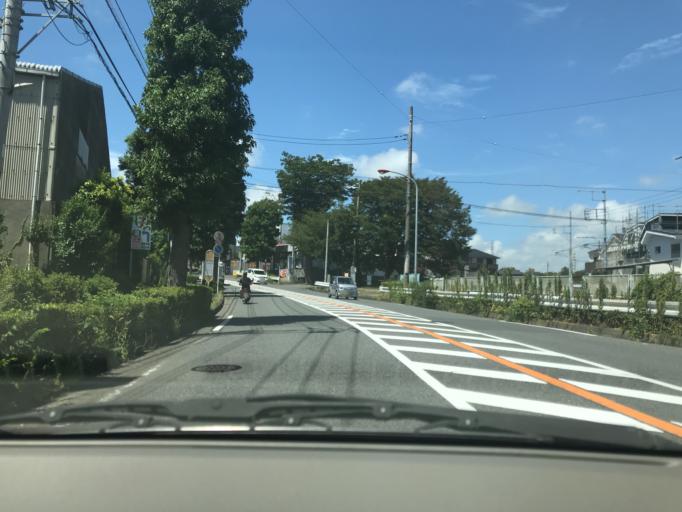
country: JP
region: Kanagawa
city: Fujisawa
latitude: 35.3595
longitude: 139.4496
